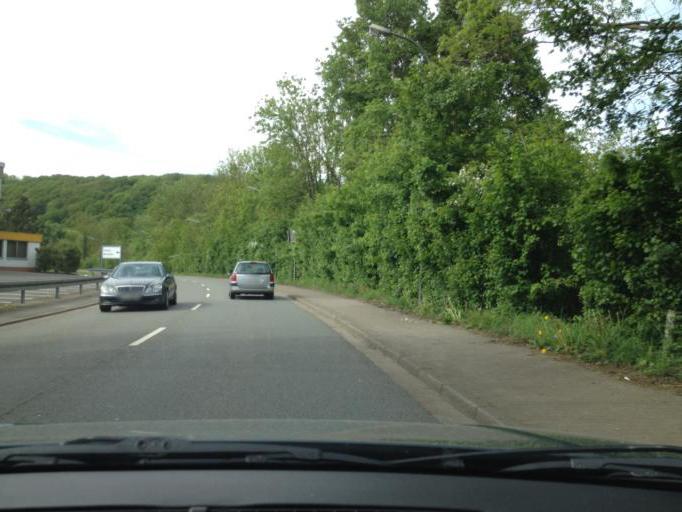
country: DE
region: Saarland
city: Bexbach
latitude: 49.3519
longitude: 7.2246
